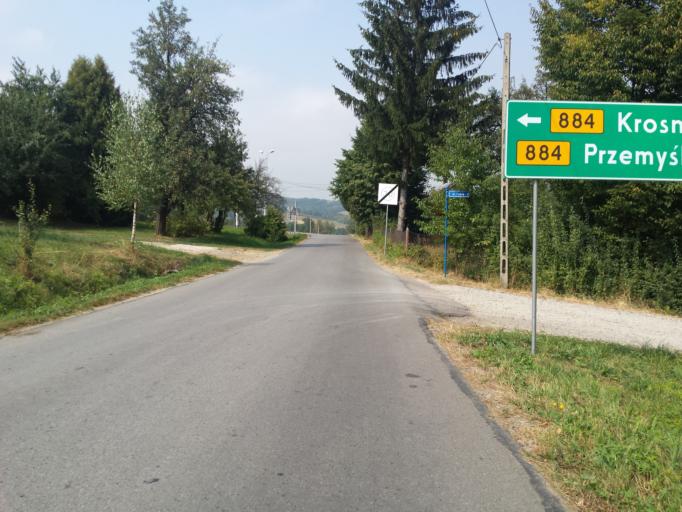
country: PL
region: Subcarpathian Voivodeship
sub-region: Powiat rzeszowski
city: Dynow
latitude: 49.8273
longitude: 22.2044
